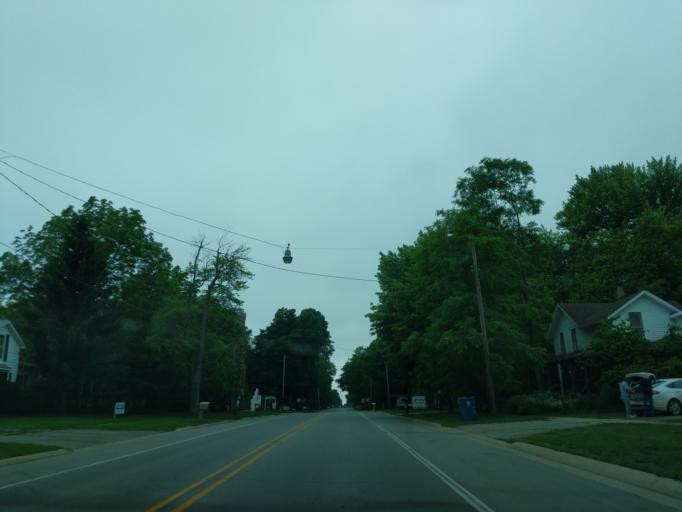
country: US
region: Michigan
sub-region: Hillsdale County
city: Litchfield
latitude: 41.9566
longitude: -84.7710
